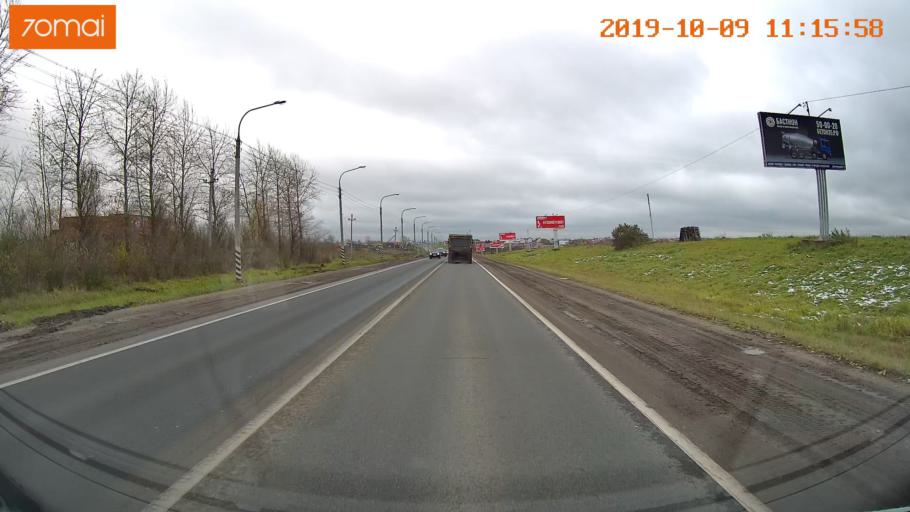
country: RU
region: Vologda
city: Vologda
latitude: 59.1795
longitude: 39.8772
